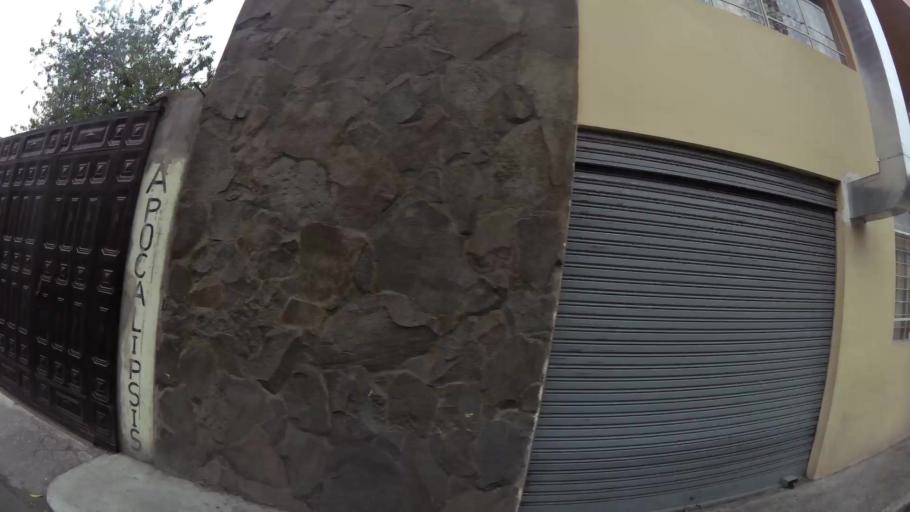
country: EC
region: Cotopaxi
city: Latacunga
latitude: -0.9305
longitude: -78.6118
